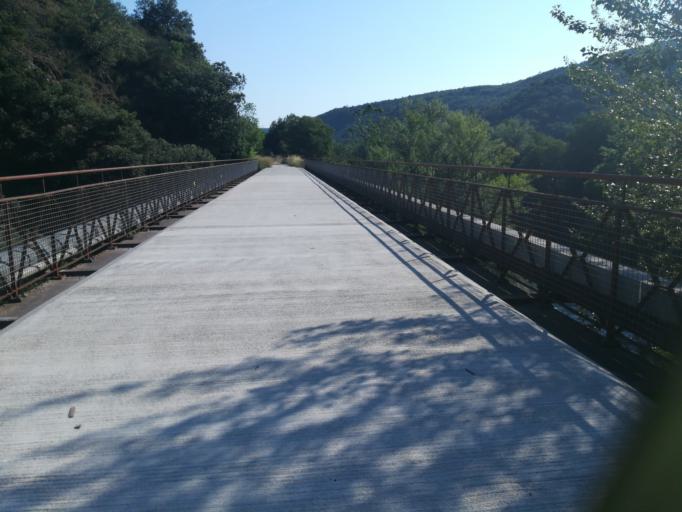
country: FR
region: Languedoc-Roussillon
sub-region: Departement des Pyrenees-Orientales
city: Reiners
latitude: 42.4852
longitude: 2.6969
